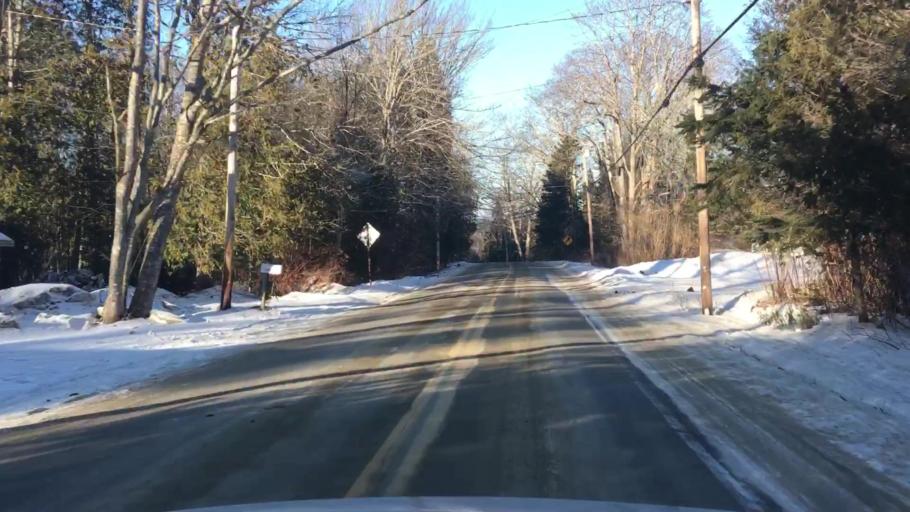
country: US
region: Maine
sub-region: Hancock County
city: Castine
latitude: 44.3770
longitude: -68.7520
